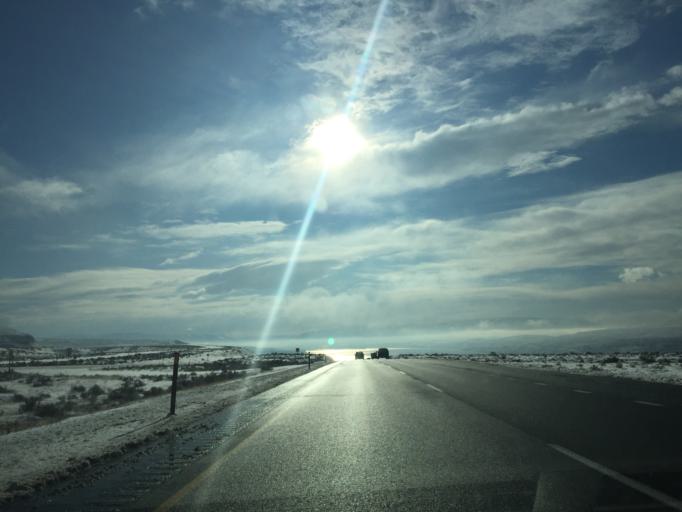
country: US
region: Washington
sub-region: Grant County
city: Mattawa
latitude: 46.9708
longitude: -119.9681
